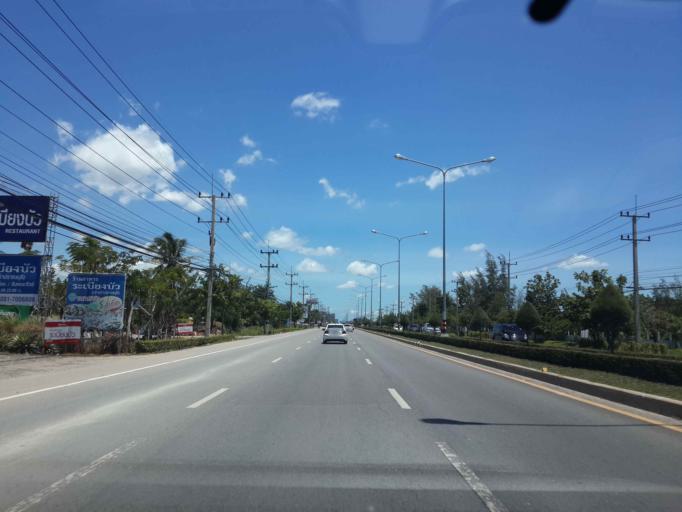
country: TH
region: Prachuap Khiri Khan
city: Hua Hin
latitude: 12.6748
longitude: 99.9525
